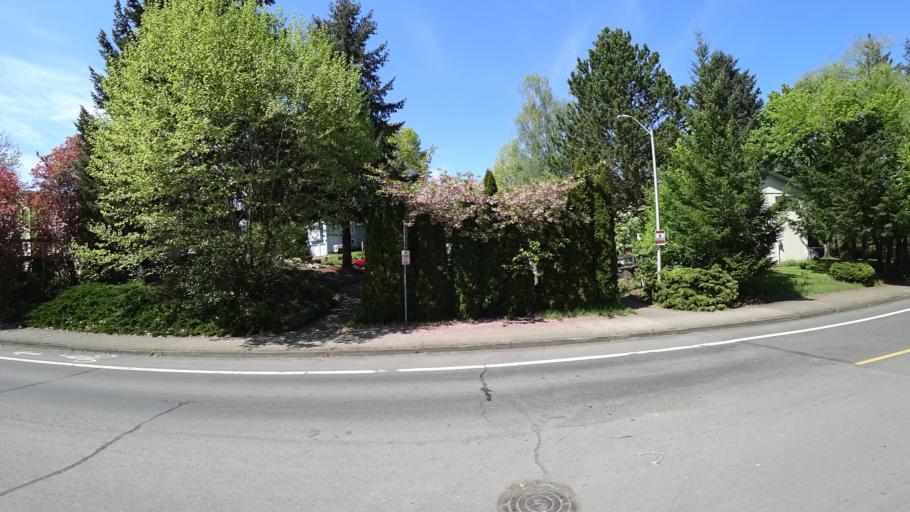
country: US
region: Oregon
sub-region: Washington County
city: Hillsboro
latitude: 45.5090
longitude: -122.9506
